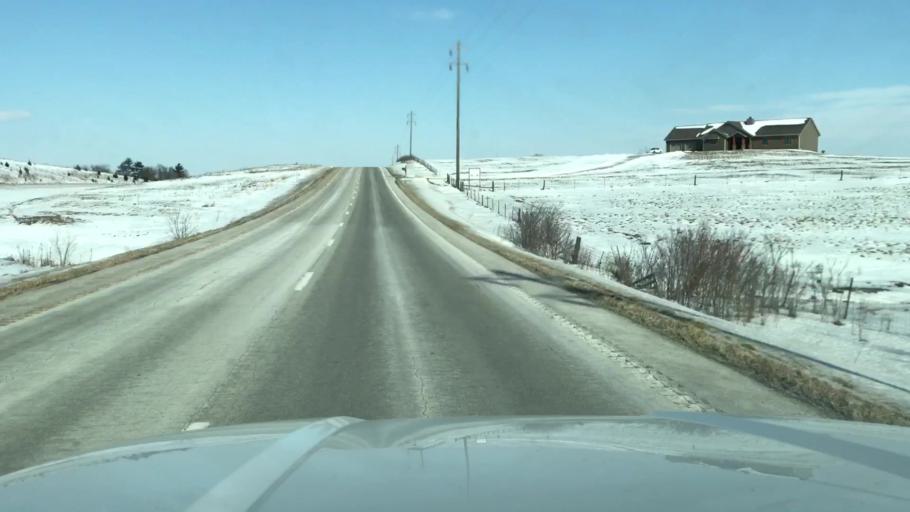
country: US
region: Missouri
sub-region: Andrew County
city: Savannah
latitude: 40.1309
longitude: -94.8695
